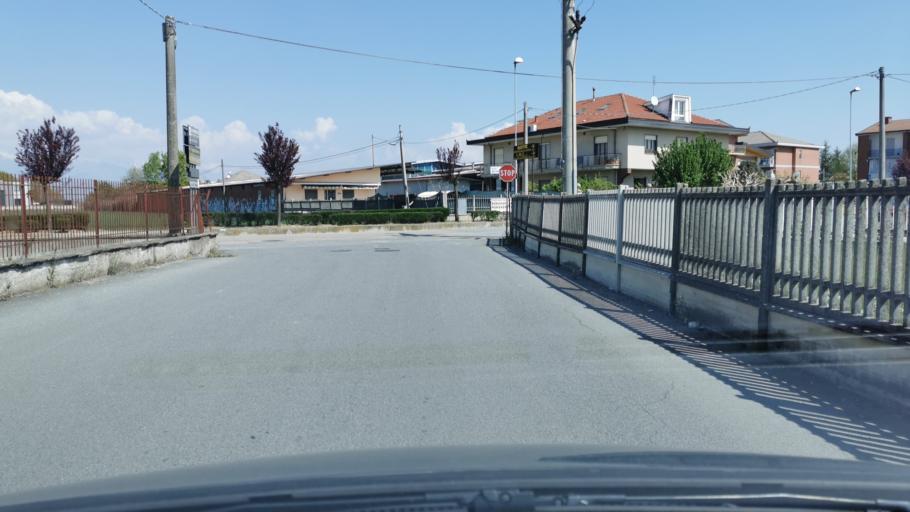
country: IT
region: Piedmont
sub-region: Provincia di Torino
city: Bosconero
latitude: 45.2671
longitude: 7.7600
